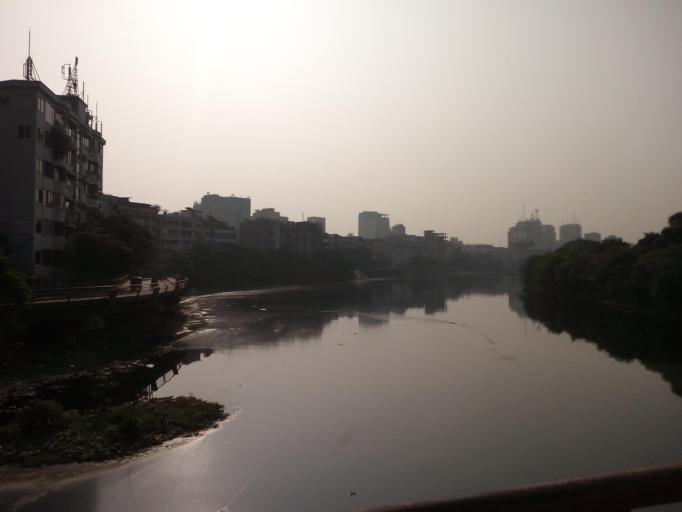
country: BD
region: Dhaka
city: Paltan
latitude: 23.7901
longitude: 90.4117
